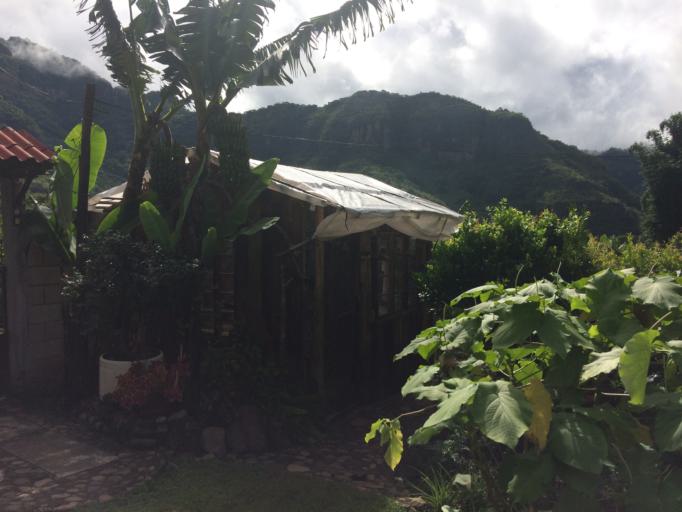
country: MX
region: Mexico
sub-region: Ocuilan
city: Plaza Nueva
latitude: 18.9431
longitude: -99.4278
